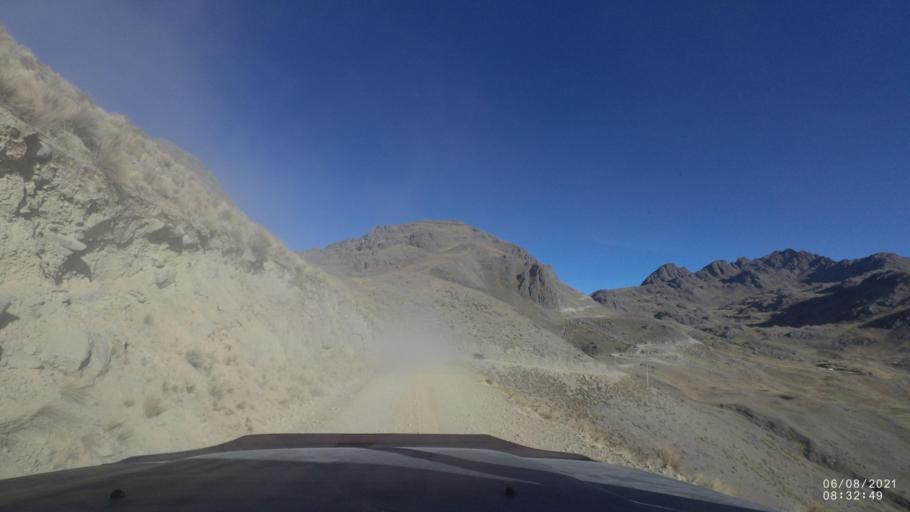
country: BO
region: Cochabamba
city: Sipe Sipe
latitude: -17.1816
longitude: -66.3747
